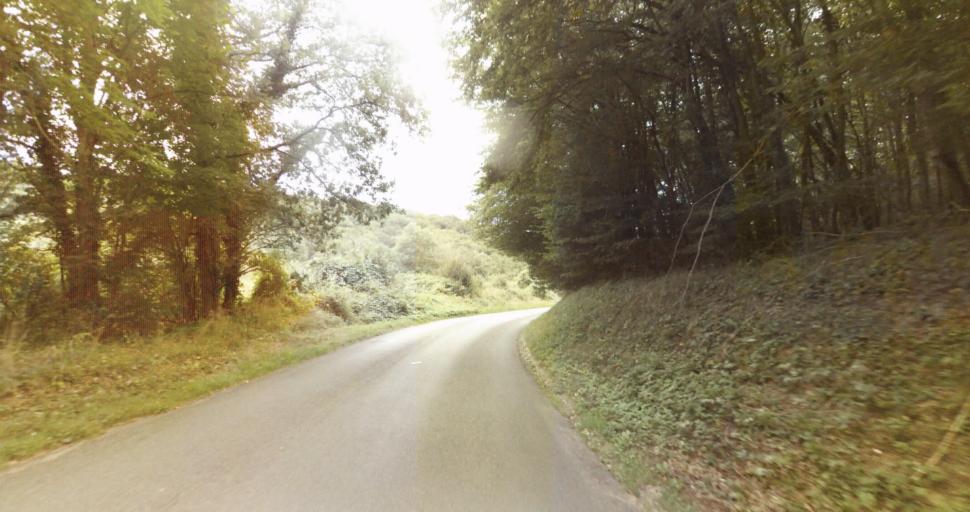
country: FR
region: Haute-Normandie
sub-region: Departement de l'Eure
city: La Couture-Boussey
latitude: 48.8812
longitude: 1.3749
